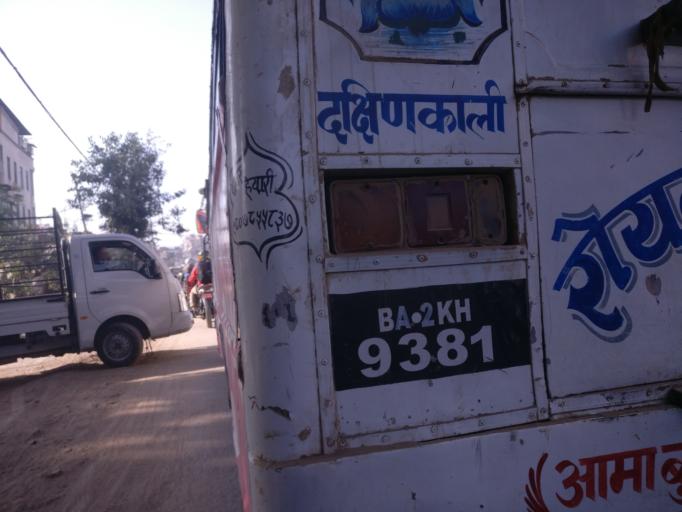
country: NP
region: Central Region
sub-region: Bagmati Zone
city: Kathmandu
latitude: 27.6970
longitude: 85.3051
